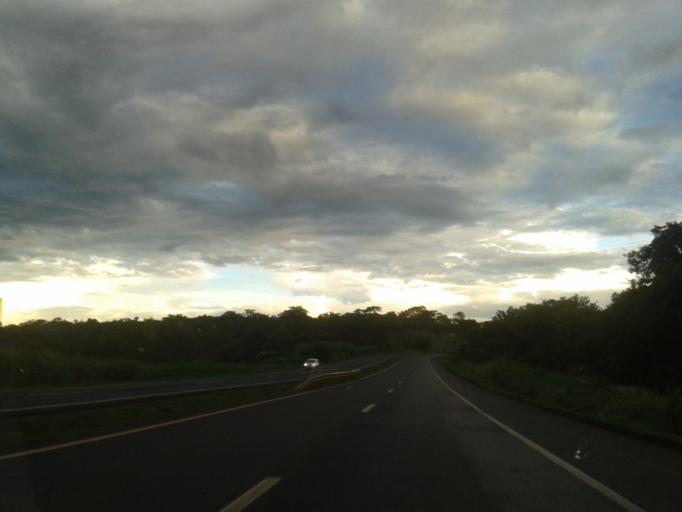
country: BR
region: Minas Gerais
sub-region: Centralina
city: Centralina
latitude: -18.6223
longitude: -49.1883
